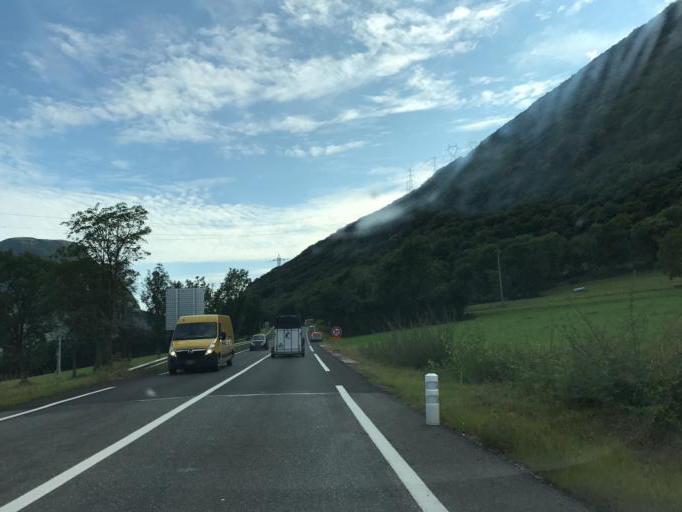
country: FR
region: Rhone-Alpes
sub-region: Departement de l'Ain
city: Collonges
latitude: 46.1322
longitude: 5.9035
